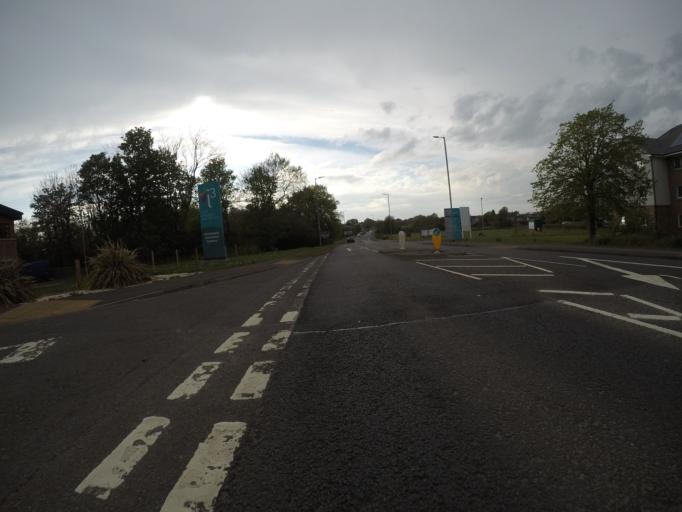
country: GB
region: Scotland
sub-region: North Ayrshire
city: Irvine
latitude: 55.6102
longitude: -4.6500
